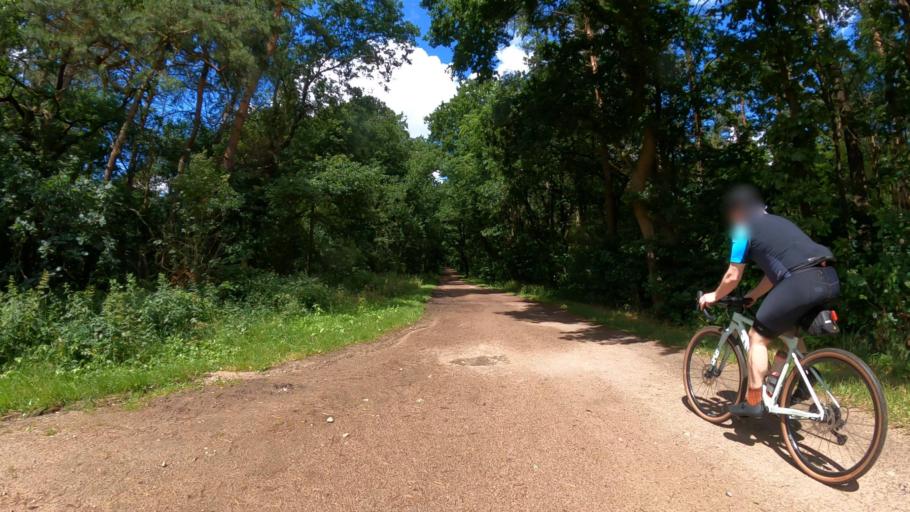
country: DE
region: Lower Saxony
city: Neu Wulmstorf
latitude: 53.4119
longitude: 9.8142
